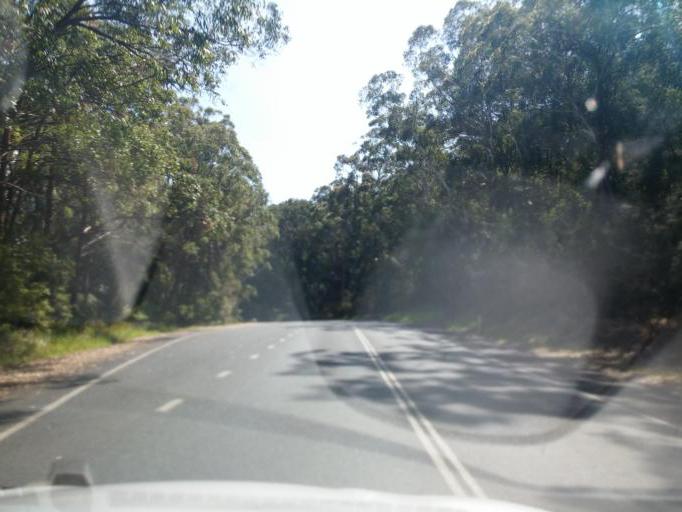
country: AU
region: New South Wales
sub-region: Great Lakes
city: Forster
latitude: -32.3157
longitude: 152.5144
